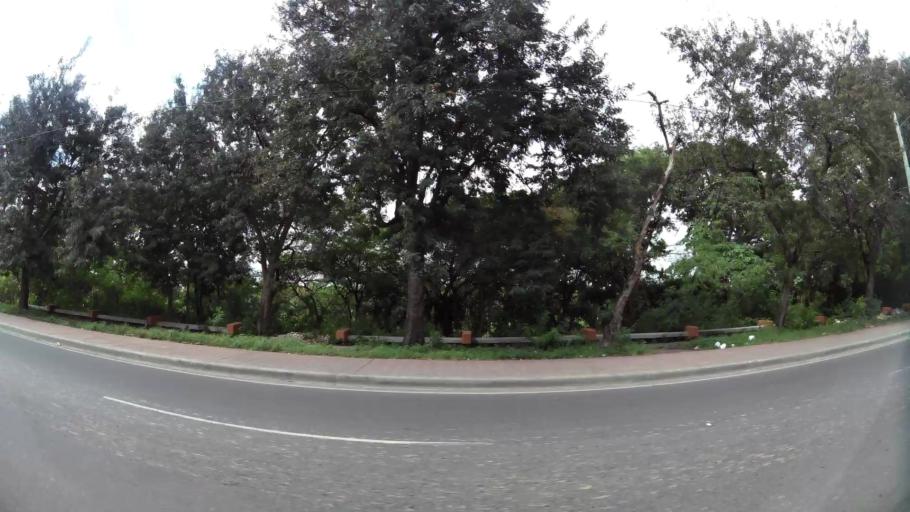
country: DO
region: Santiago
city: Santiago de los Caballeros
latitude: 19.4705
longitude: -70.7167
